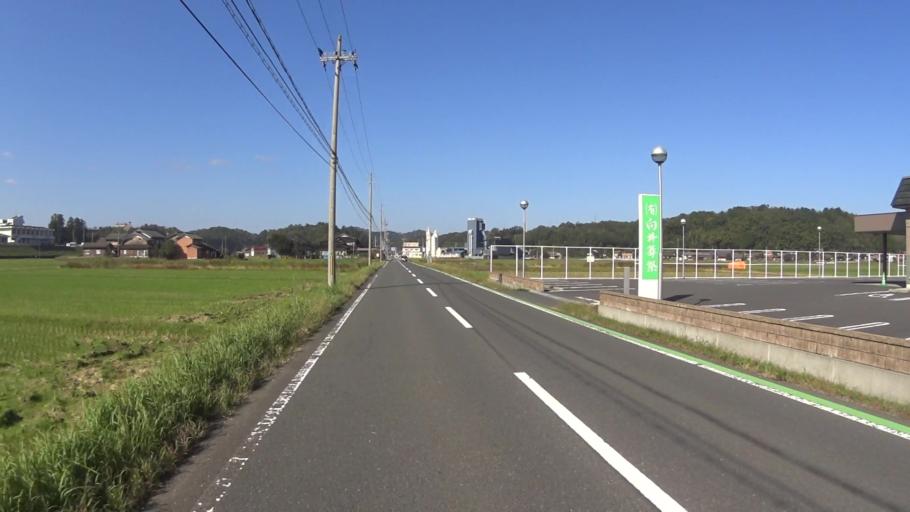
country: JP
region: Kyoto
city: Miyazu
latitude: 35.6702
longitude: 135.0850
